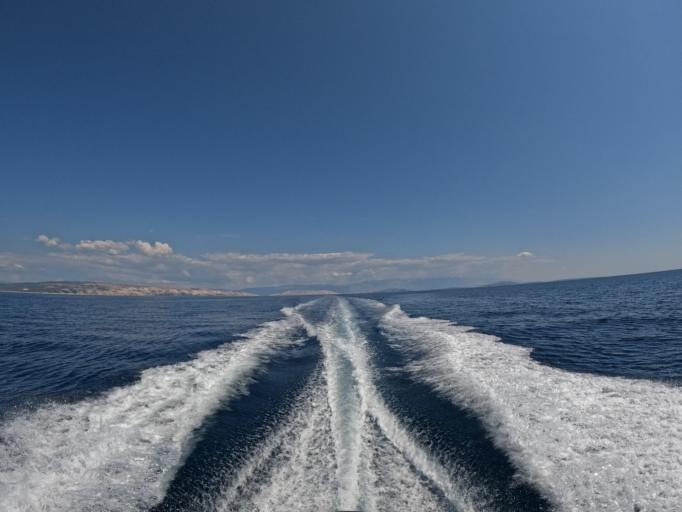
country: HR
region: Primorsko-Goranska
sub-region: Grad Krk
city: Krk
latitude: 44.9253
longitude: 14.5407
